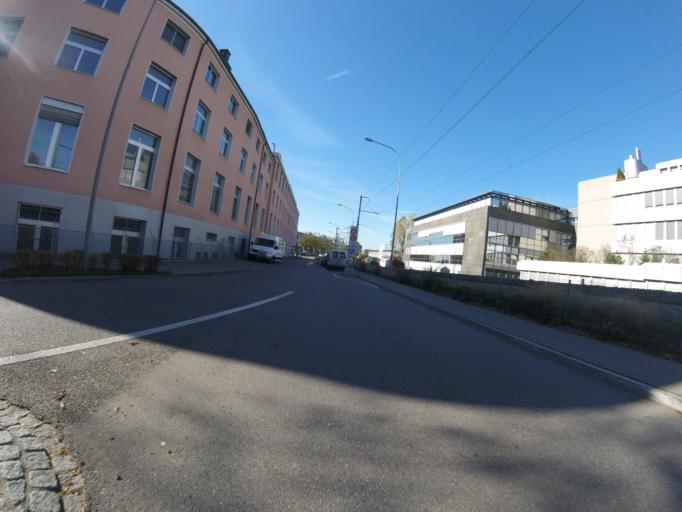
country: CH
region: Bern
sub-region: Bern-Mittelland District
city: Muri
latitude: 46.9329
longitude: 7.5094
